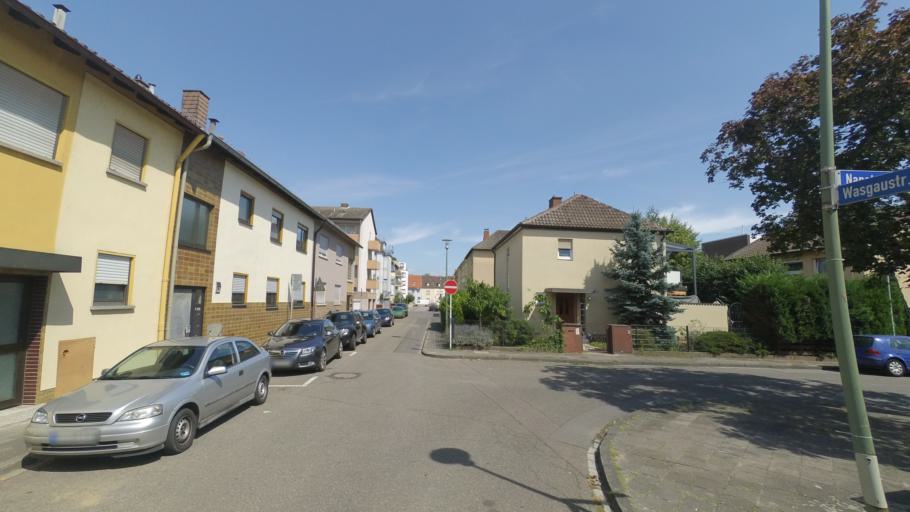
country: DE
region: Rheinland-Pfalz
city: Gartenstadt
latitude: 49.4583
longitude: 8.4262
